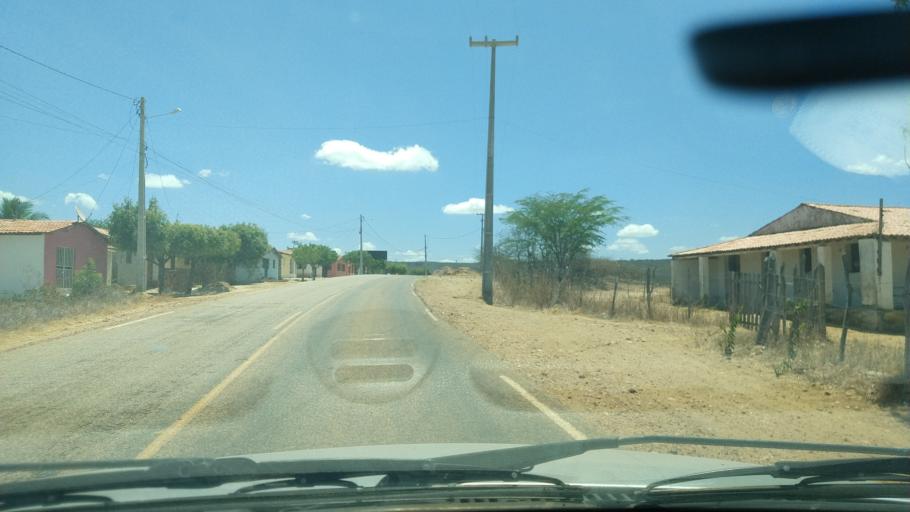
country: BR
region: Rio Grande do Norte
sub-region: Cerro Cora
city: Cerro Cora
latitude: -6.0592
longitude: -36.3618
